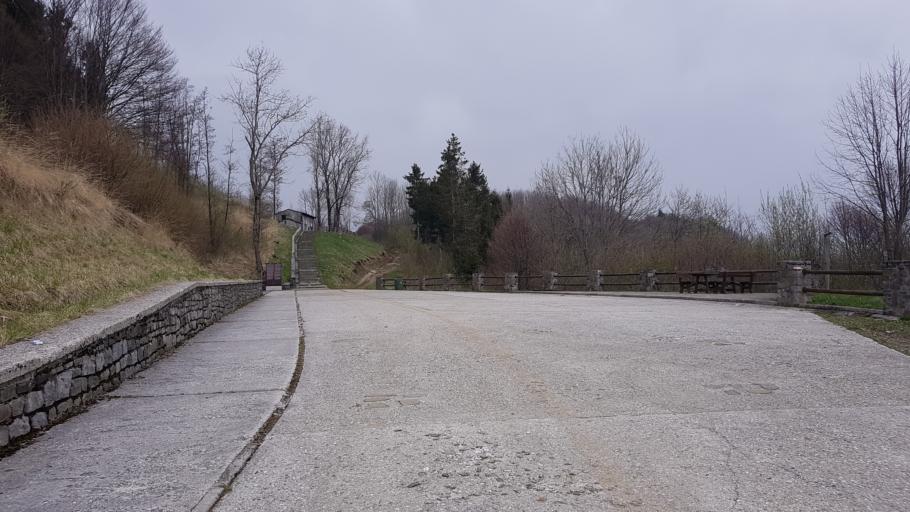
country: IT
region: Friuli Venezia Giulia
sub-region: Provincia di Udine
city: Faedis
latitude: 46.1886
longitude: 13.3839
